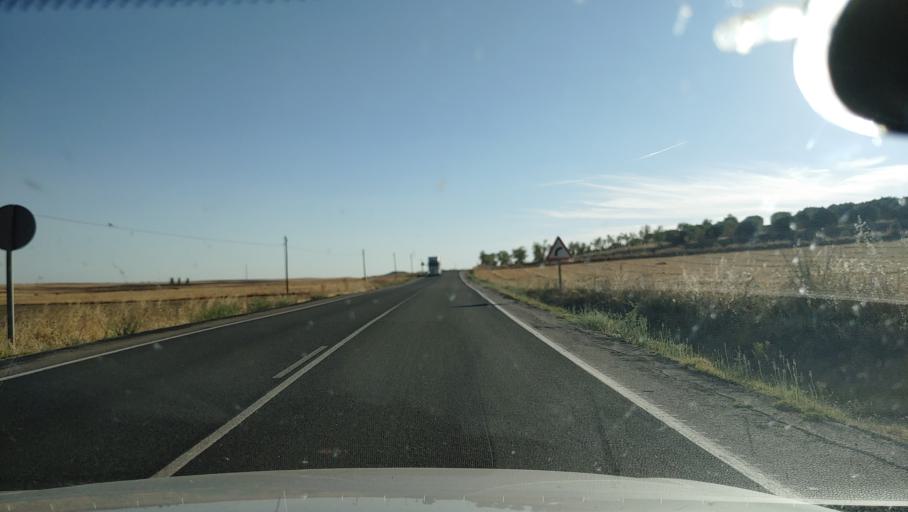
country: ES
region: Castille-La Mancha
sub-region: Provincia de Ciudad Real
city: Fuenllana
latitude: 38.7642
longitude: -2.9337
